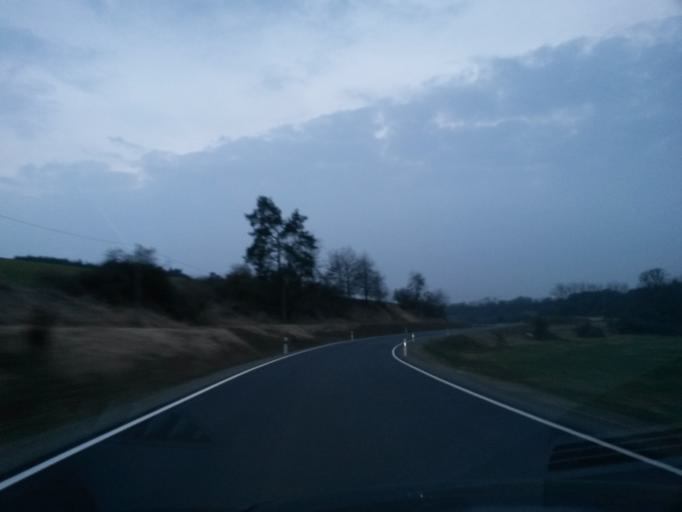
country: DE
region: Bavaria
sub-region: Regierungsbezirk Unterfranken
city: Massbach
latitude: 50.1865
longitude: 10.2959
